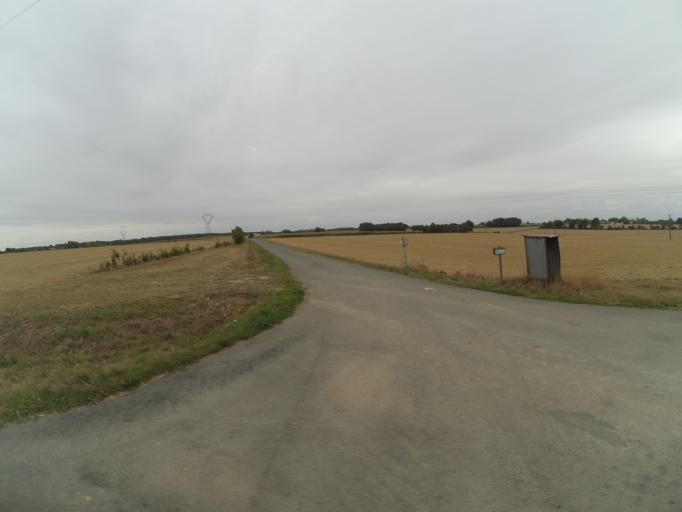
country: FR
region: Pays de la Loire
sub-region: Departement de la Vendee
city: Saint-Andre-Treize-Voies
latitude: 46.9209
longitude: -1.3923
